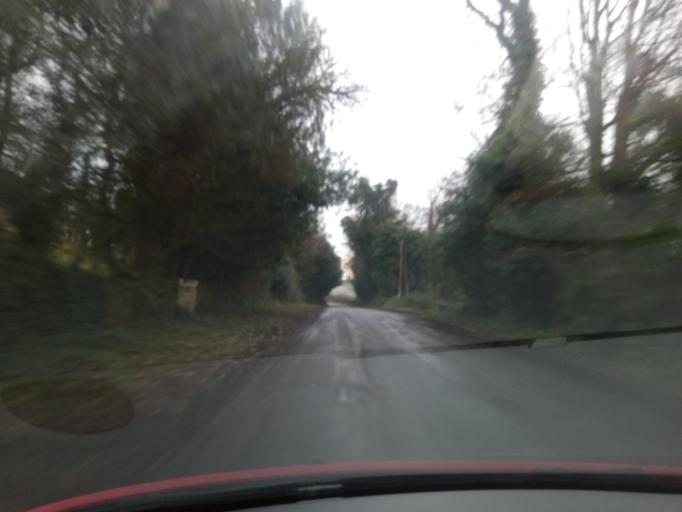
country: GB
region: England
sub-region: Northumberland
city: Whittingham
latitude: 55.4862
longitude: -1.8945
